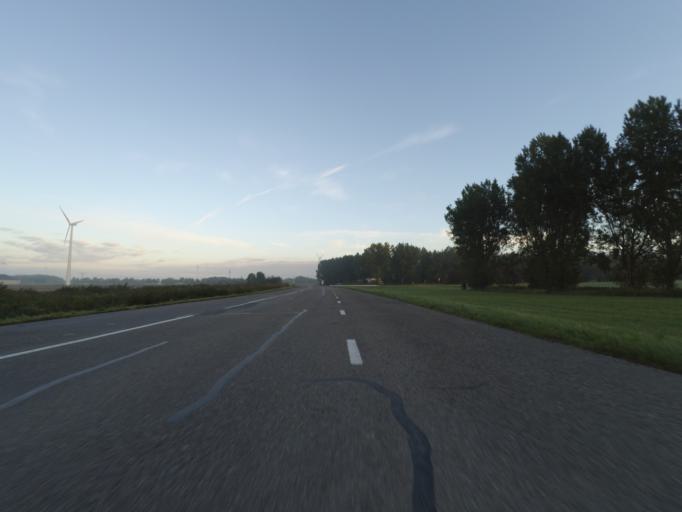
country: NL
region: Utrecht
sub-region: Gemeente Bunschoten
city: Bunschoten
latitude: 52.3247
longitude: 5.4281
